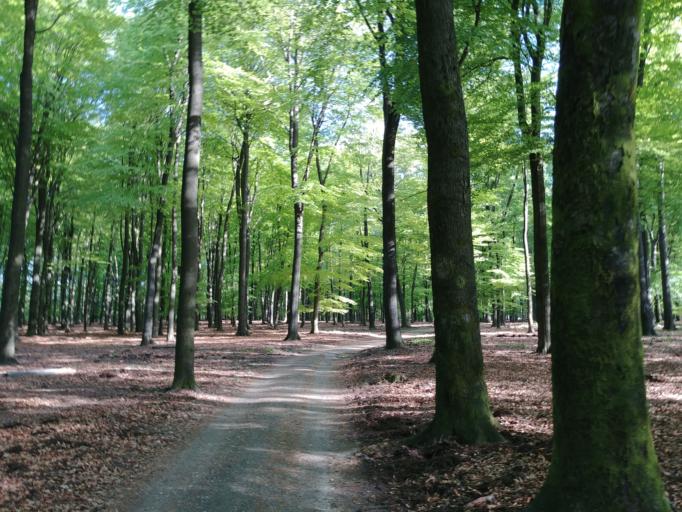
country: NL
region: Gelderland
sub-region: Gemeente Apeldoorn
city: Apeldoorn
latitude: 52.2425
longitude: 5.8836
